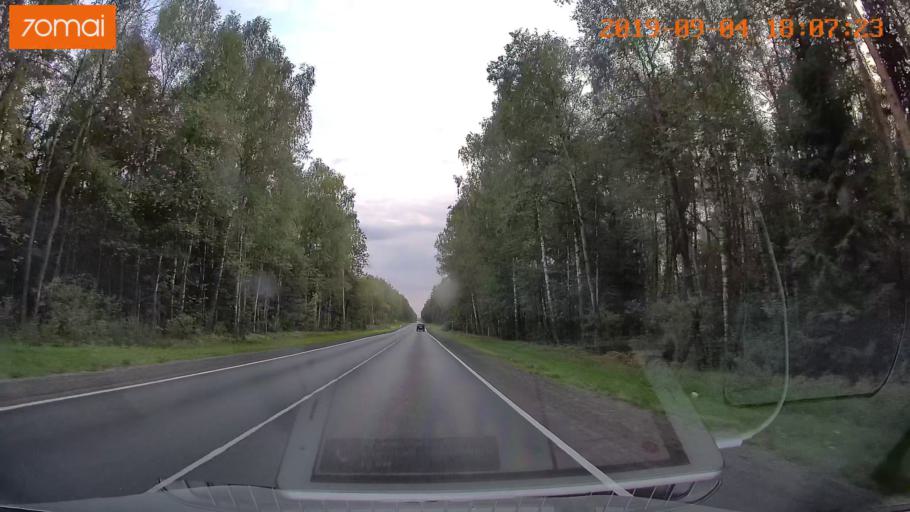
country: RU
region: Moskovskaya
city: Khorlovo
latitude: 55.4196
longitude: 38.8015
